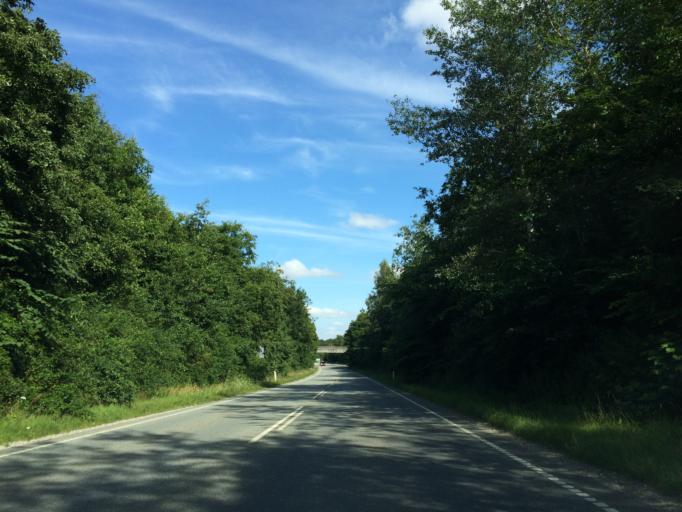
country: DK
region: Central Jutland
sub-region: Arhus Kommune
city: Logten
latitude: 56.2883
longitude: 10.3224
